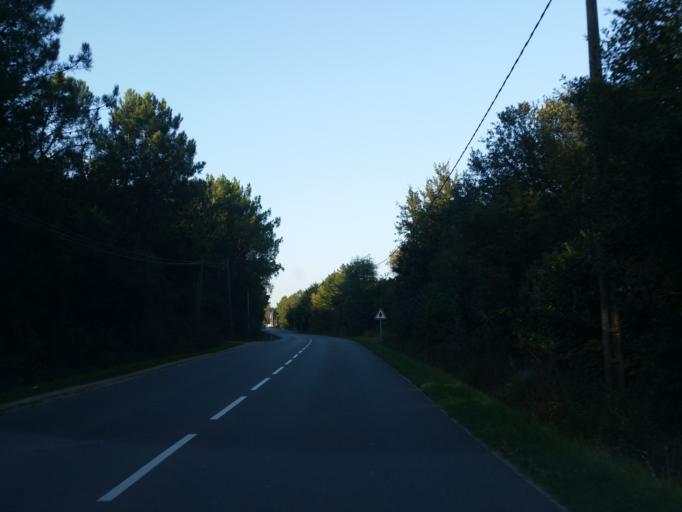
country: FR
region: Brittany
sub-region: Departement du Morbihan
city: Carnac
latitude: 47.5998
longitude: -3.0721
